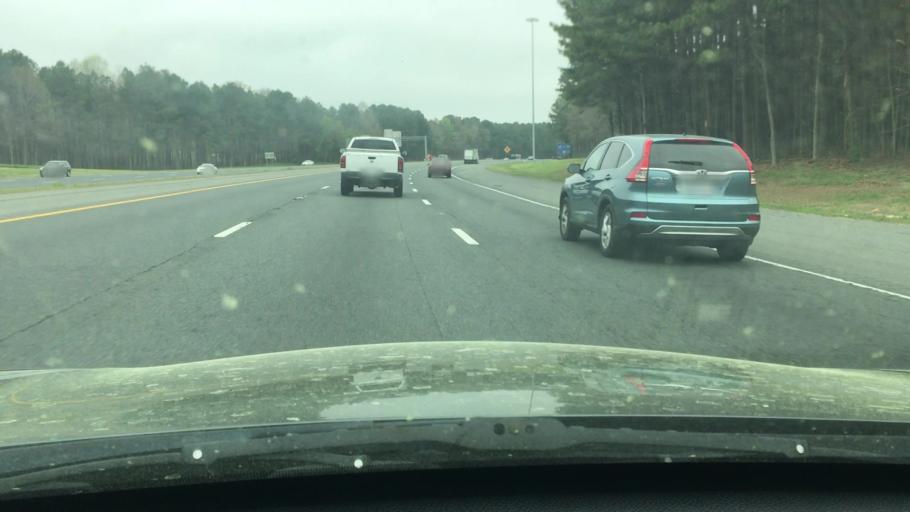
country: US
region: North Carolina
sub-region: Wake County
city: Cary
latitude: 35.7813
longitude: -78.7488
